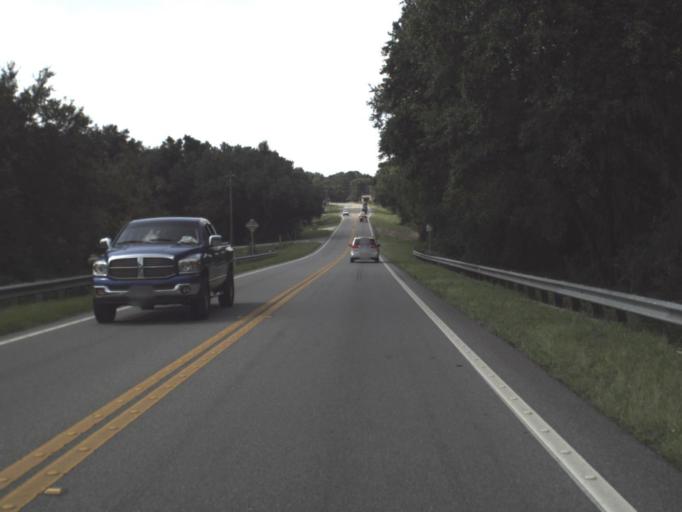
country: US
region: Florida
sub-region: Citrus County
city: Inverness
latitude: 28.8531
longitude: -82.3451
